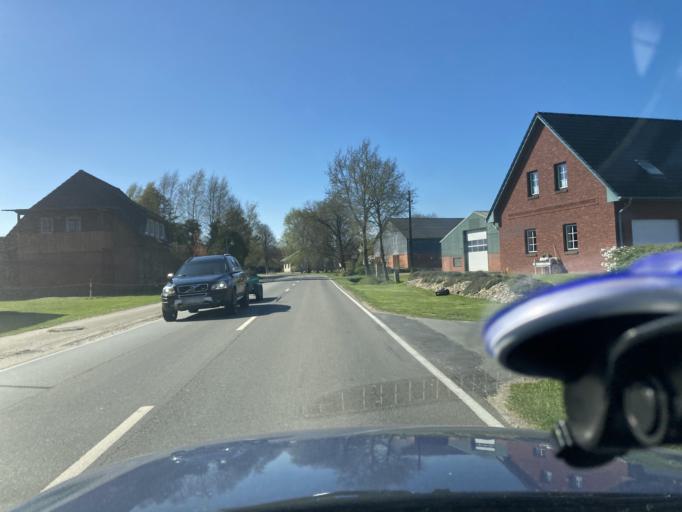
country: DE
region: Schleswig-Holstein
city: Odderade
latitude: 54.1408
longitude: 9.1908
